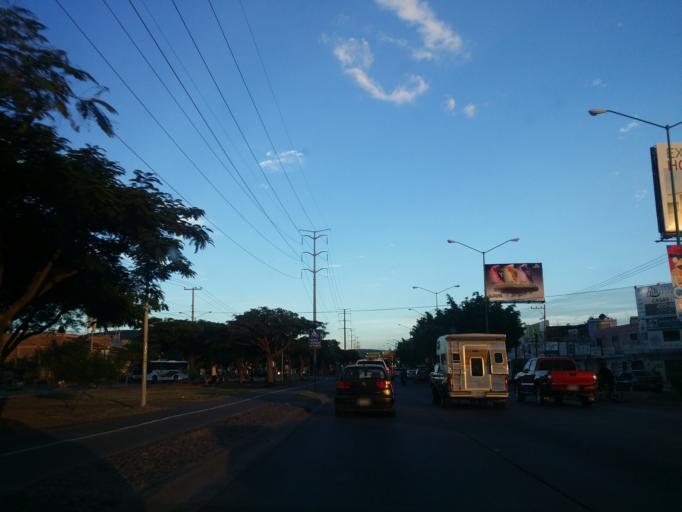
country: MX
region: Guanajuato
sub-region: Leon
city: Medina
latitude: 21.1450
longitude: -101.6468
